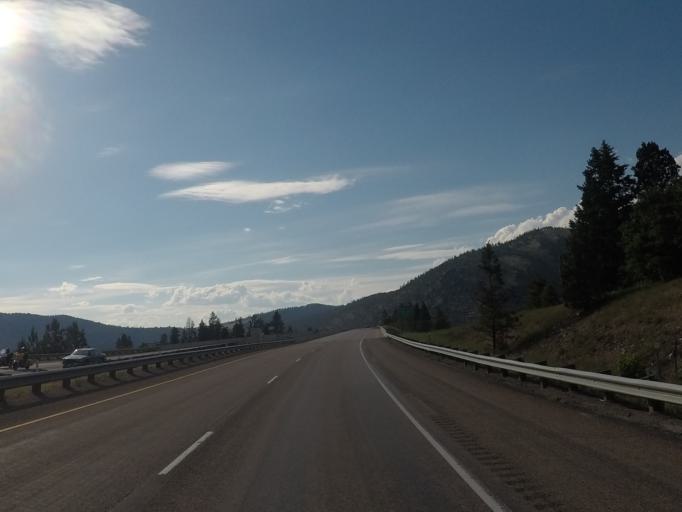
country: US
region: Montana
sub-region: Missoula County
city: Bonner-West Riverside
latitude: 46.8710
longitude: -113.8855
